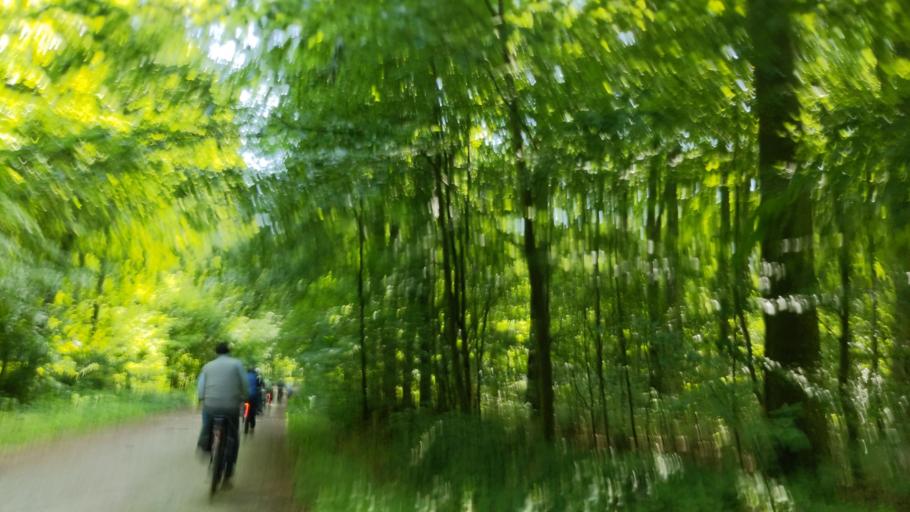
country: DE
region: Schleswig-Holstein
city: Albsfelde
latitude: 53.6891
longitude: 10.6940
